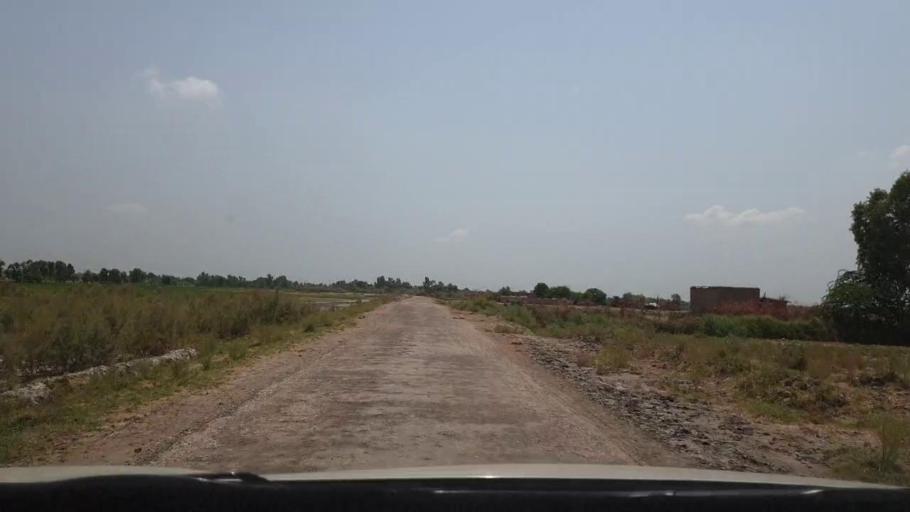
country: PK
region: Sindh
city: New Badah
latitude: 27.2997
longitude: 68.0622
